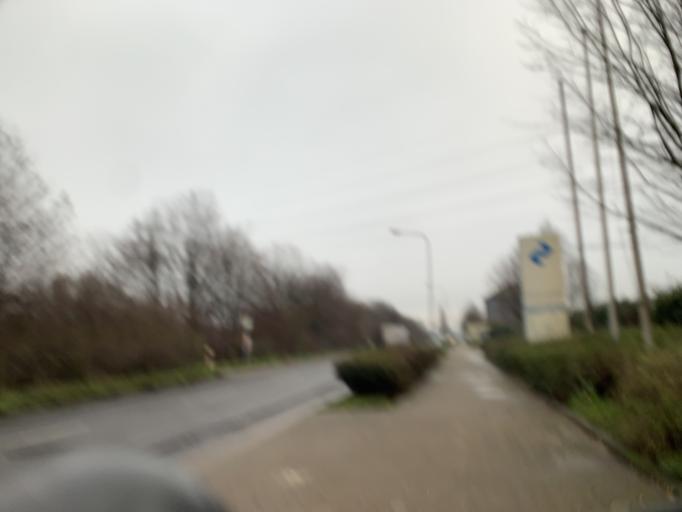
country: DE
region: North Rhine-Westphalia
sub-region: Regierungsbezirk Dusseldorf
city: Meerbusch
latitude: 51.3355
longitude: 6.6901
